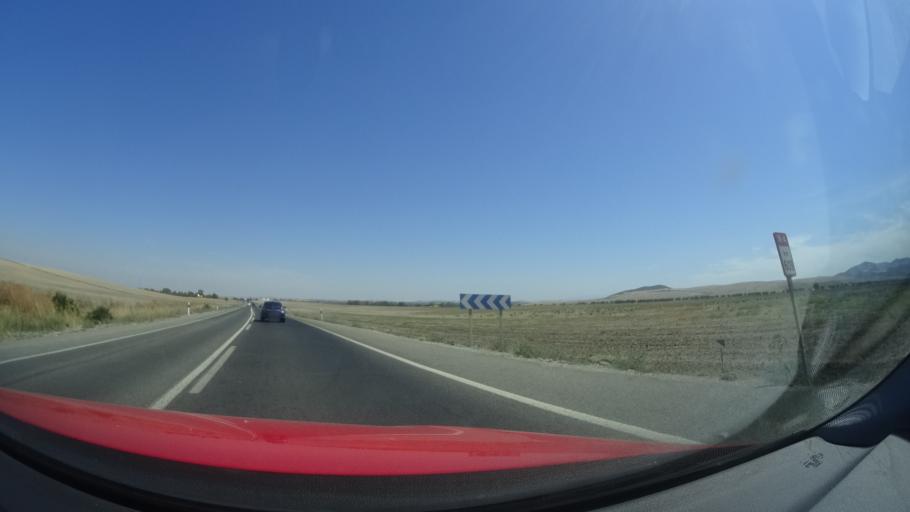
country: ES
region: Andalusia
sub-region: Provincia de Sevilla
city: Lebrija
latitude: 36.8970
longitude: -5.9944
